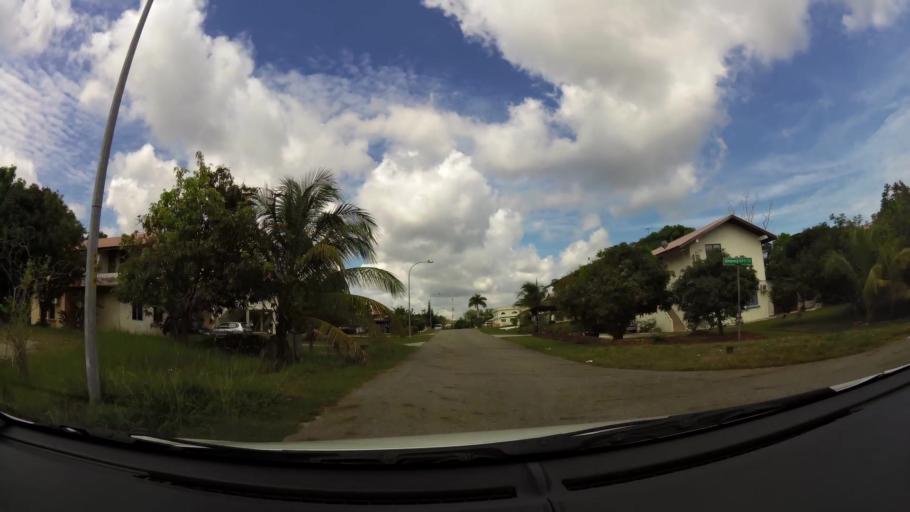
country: BN
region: Brunei and Muara
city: Bandar Seri Begawan
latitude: 4.9370
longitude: 114.8988
